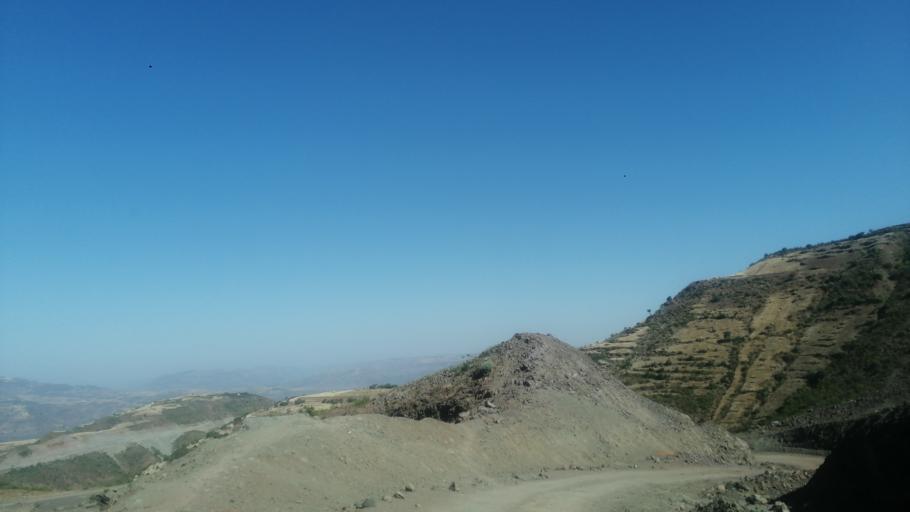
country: ET
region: Amhara
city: Addiet Canna
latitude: 11.1531
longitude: 37.8515
